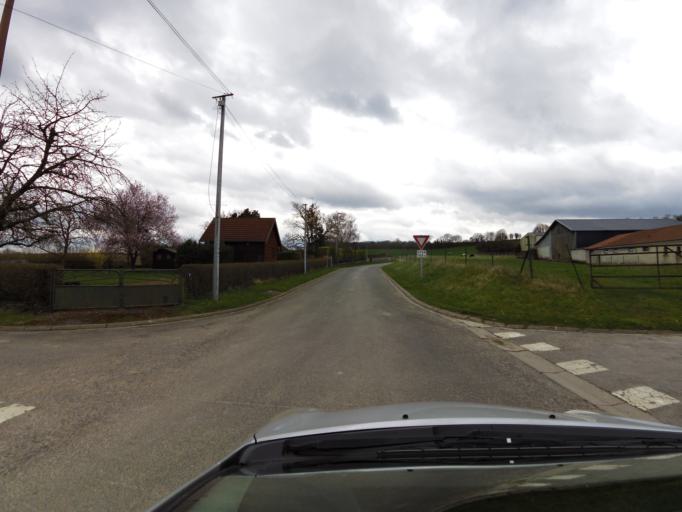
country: FR
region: Picardie
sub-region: Departement de la Somme
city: Bray-sur-Somme
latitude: 49.9394
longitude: 2.8188
